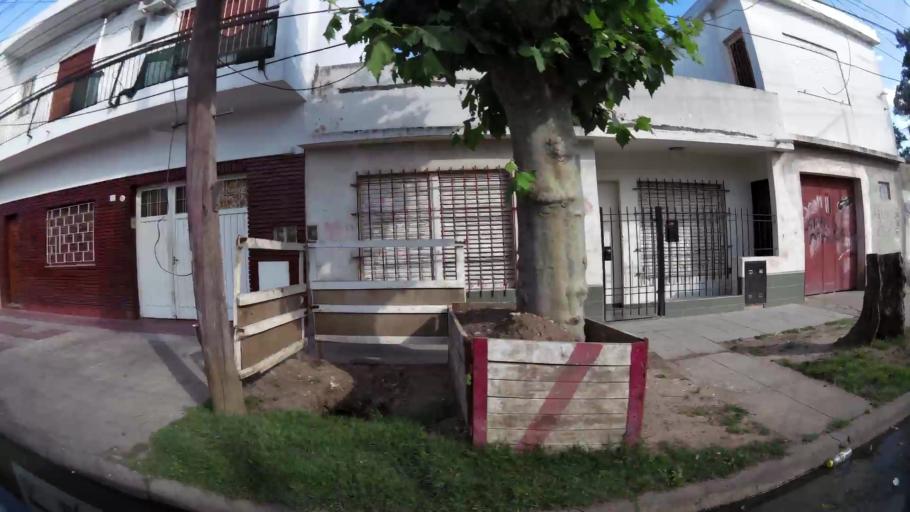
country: AR
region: Buenos Aires
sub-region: Partido de General San Martin
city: General San Martin
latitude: -34.5500
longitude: -58.5410
